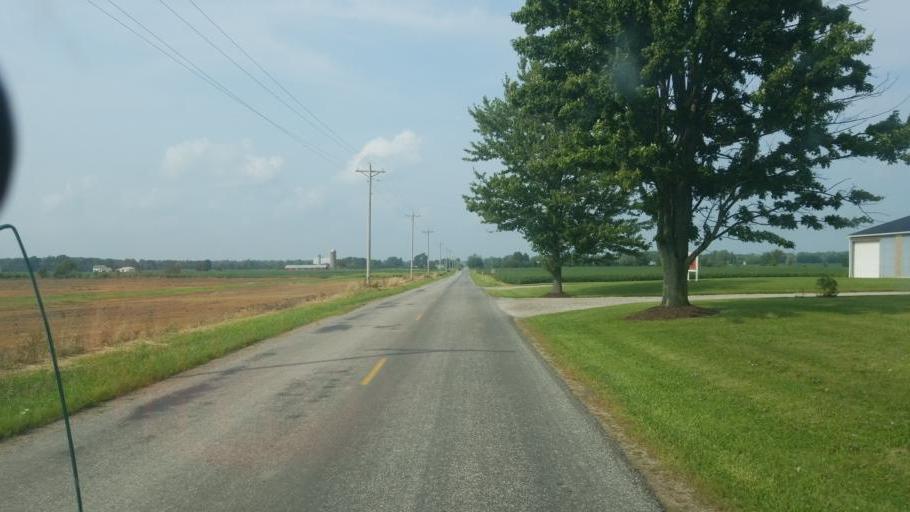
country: US
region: Ohio
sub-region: Lorain County
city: Wellington
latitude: 41.1096
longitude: -82.1611
